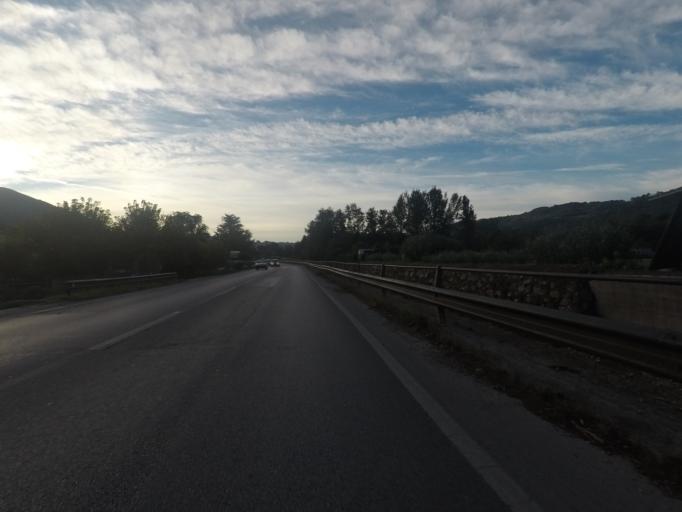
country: IT
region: Tuscany
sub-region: Provincia di Lucca
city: Corsanico-Bargecchia
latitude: 43.9364
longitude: 10.3034
